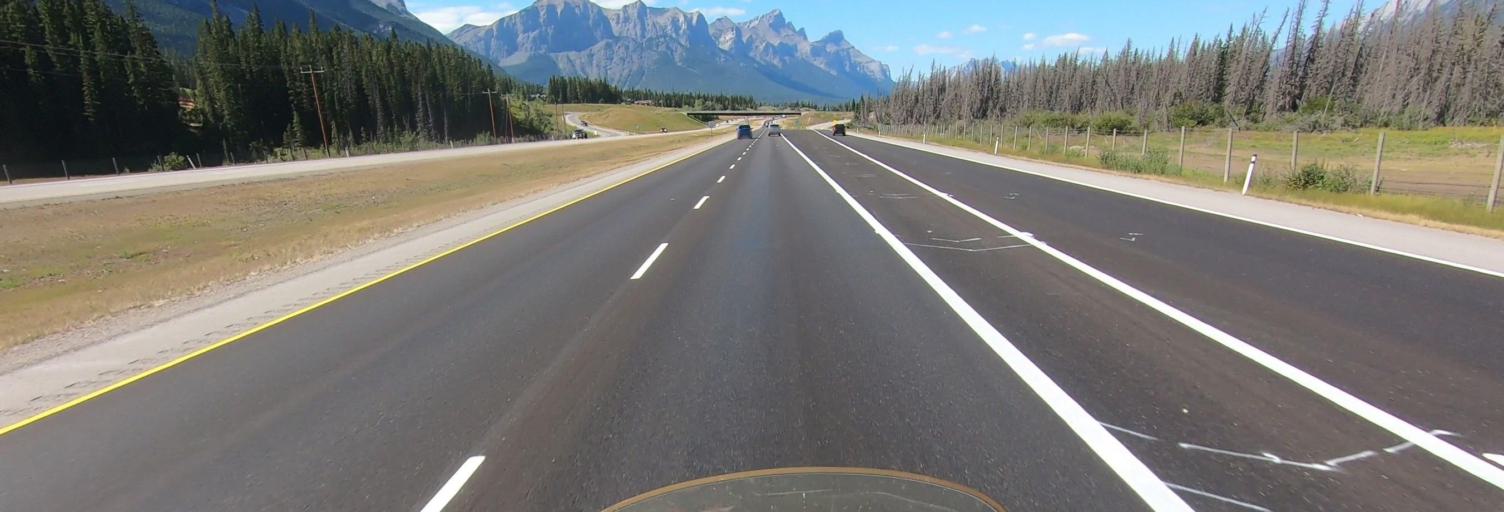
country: CA
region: Alberta
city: Canmore
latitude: 51.0525
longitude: -115.3054
